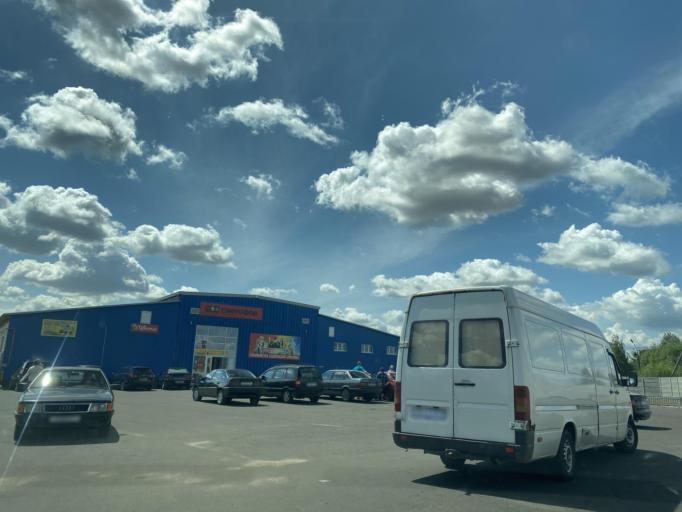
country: BY
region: Brest
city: Ivanava
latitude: 52.1380
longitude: 25.5521
